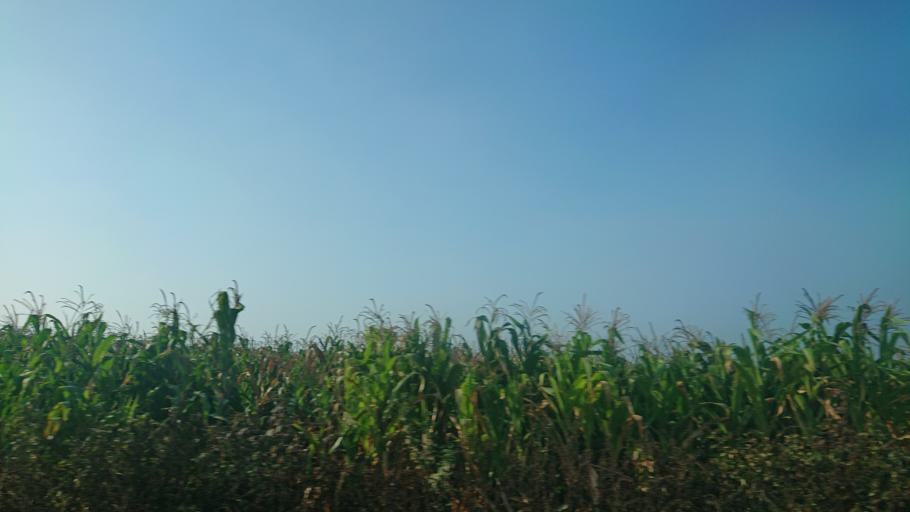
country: TW
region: Taiwan
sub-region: Tainan
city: Tainan
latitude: 23.1254
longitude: 120.2258
